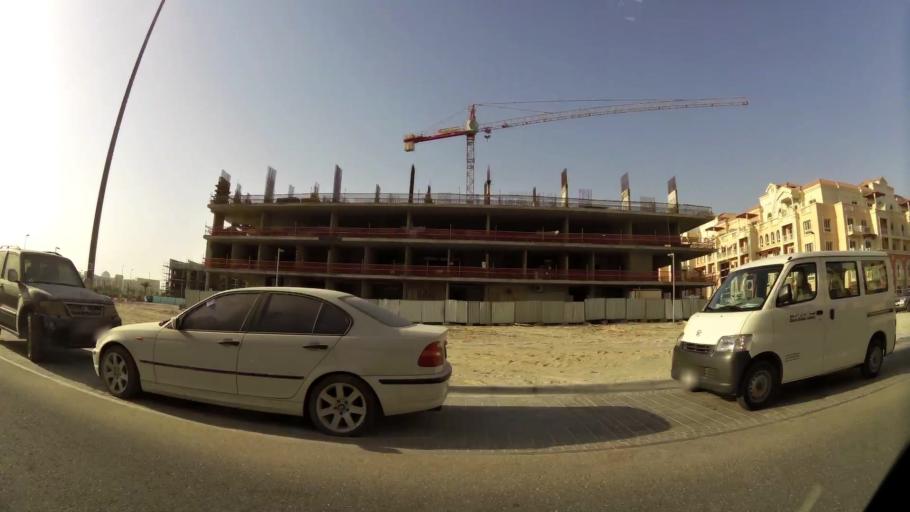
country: AE
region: Dubai
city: Dubai
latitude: 25.0622
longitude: 55.2075
